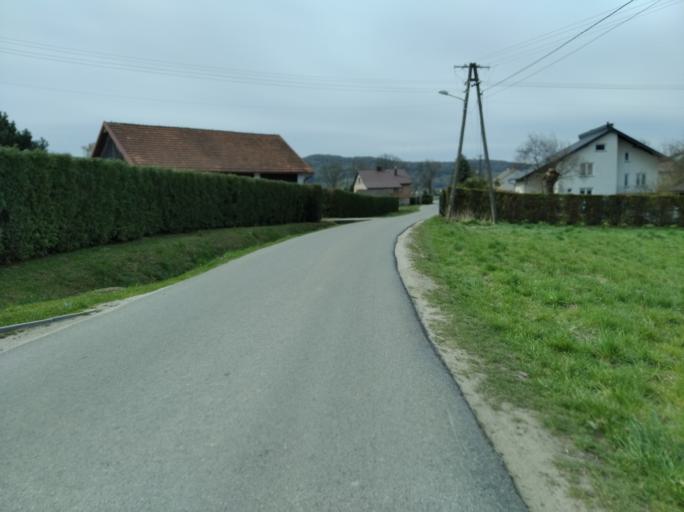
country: PL
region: Subcarpathian Voivodeship
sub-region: Powiat strzyzowski
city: Wisniowa
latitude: 49.8732
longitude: 21.6676
